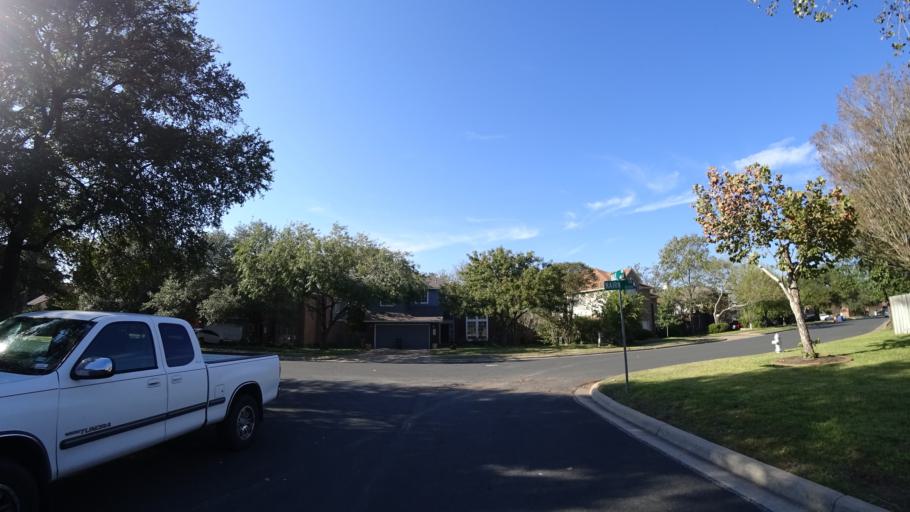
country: US
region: Texas
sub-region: Travis County
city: Shady Hollow
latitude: 30.2088
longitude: -97.8572
